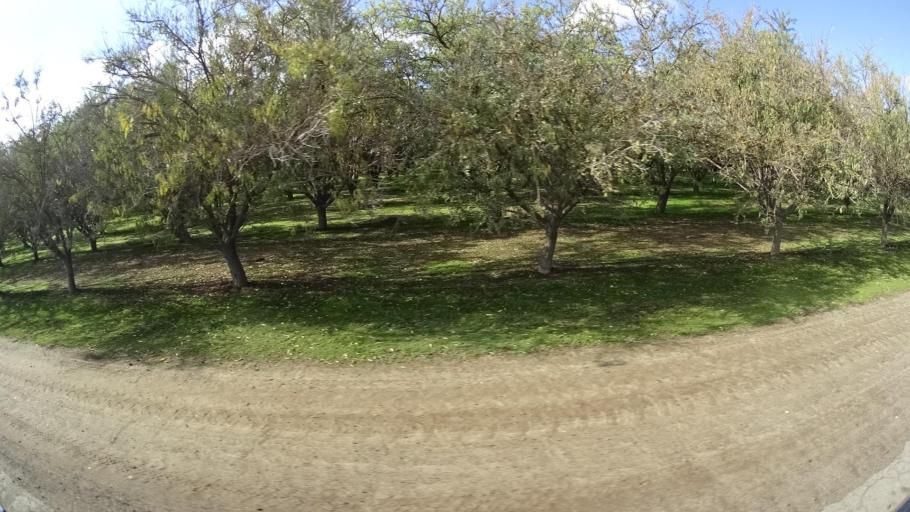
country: US
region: California
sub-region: Kern County
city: McFarland
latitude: 35.6774
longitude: -119.2676
